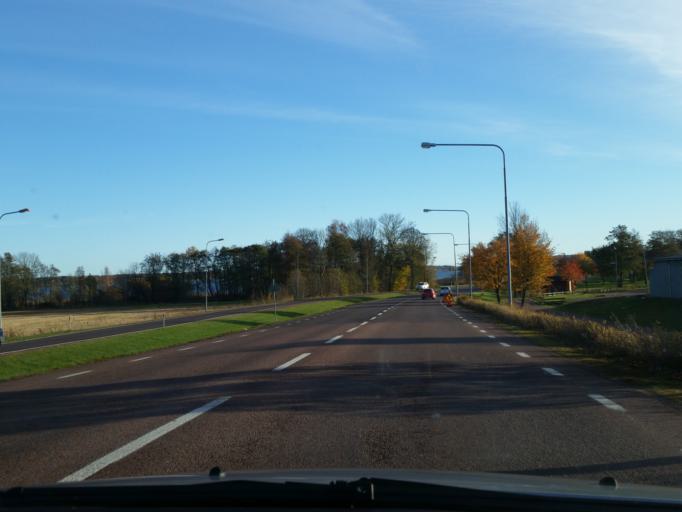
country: AX
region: Mariehamns stad
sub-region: Mariehamn
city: Mariehamn
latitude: 60.1133
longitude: 19.9410
